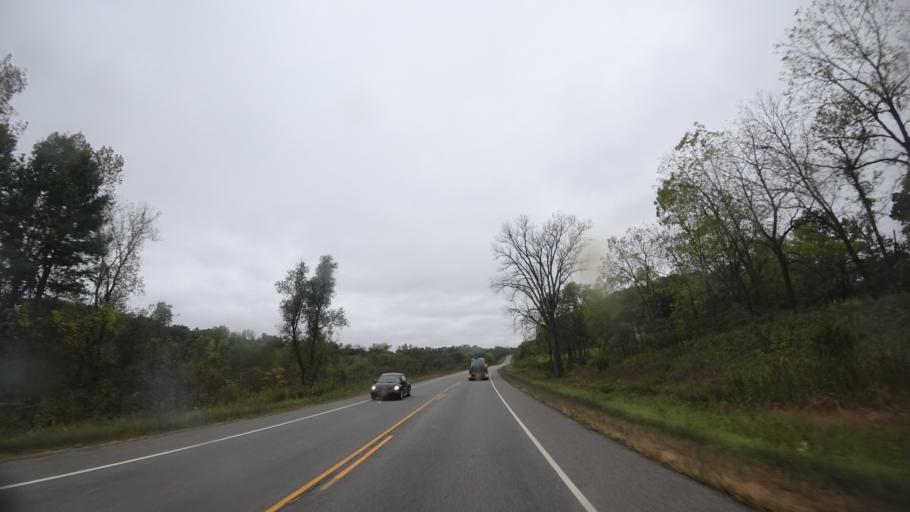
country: US
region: Wisconsin
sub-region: Crawford County
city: Prairie du Chien
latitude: 43.0128
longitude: -91.0413
